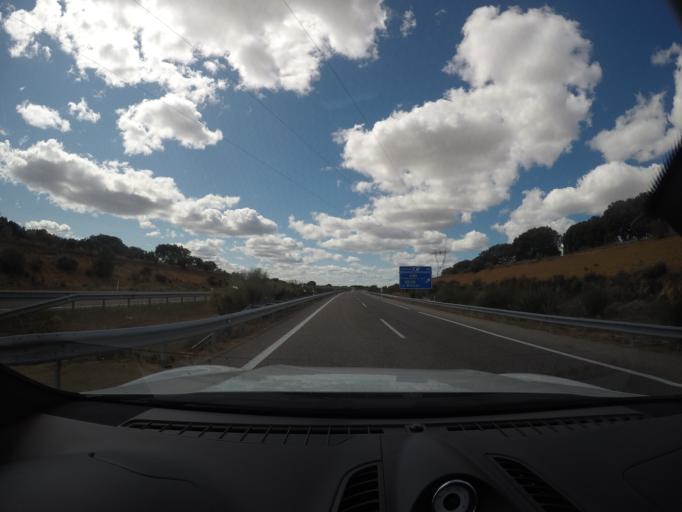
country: ES
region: Castille and Leon
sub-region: Provincia de Zamora
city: Camarzana de Tera
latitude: 42.0070
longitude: -5.9992
